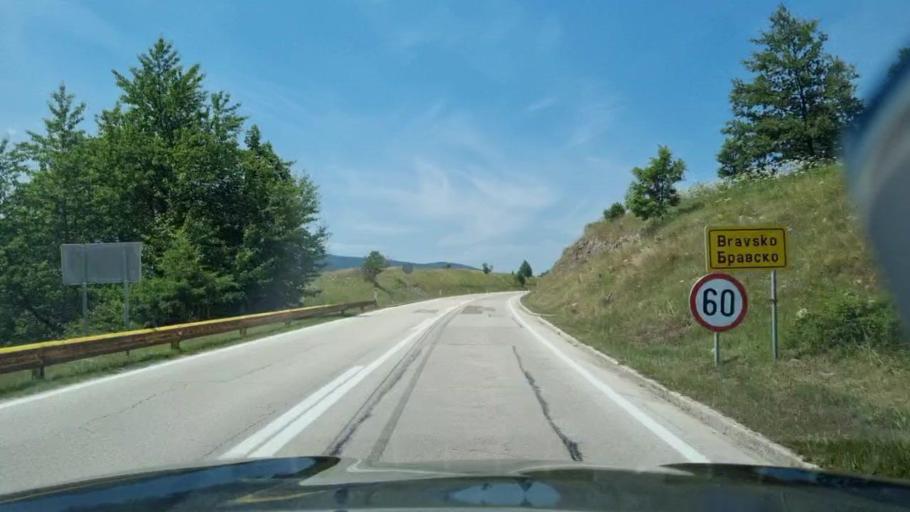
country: BA
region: Federation of Bosnia and Herzegovina
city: Sanica
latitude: 44.5479
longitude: 16.5884
